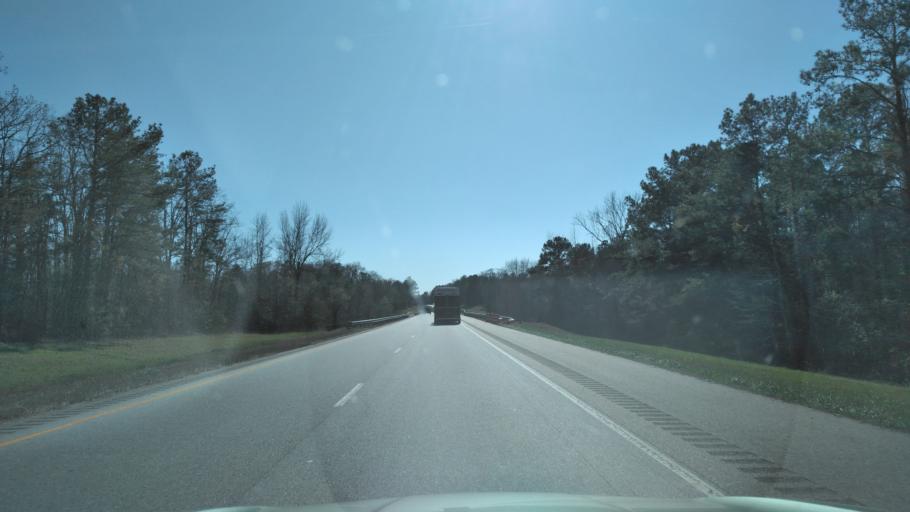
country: US
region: Alabama
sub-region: Lowndes County
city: Fort Deposit
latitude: 32.0560
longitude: -86.4952
